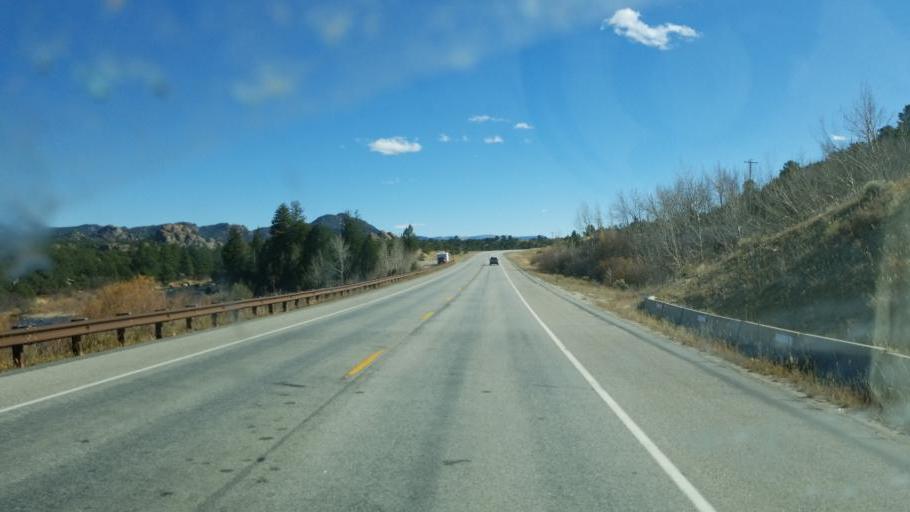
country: US
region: Colorado
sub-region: Chaffee County
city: Buena Vista
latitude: 38.8913
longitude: -106.1706
